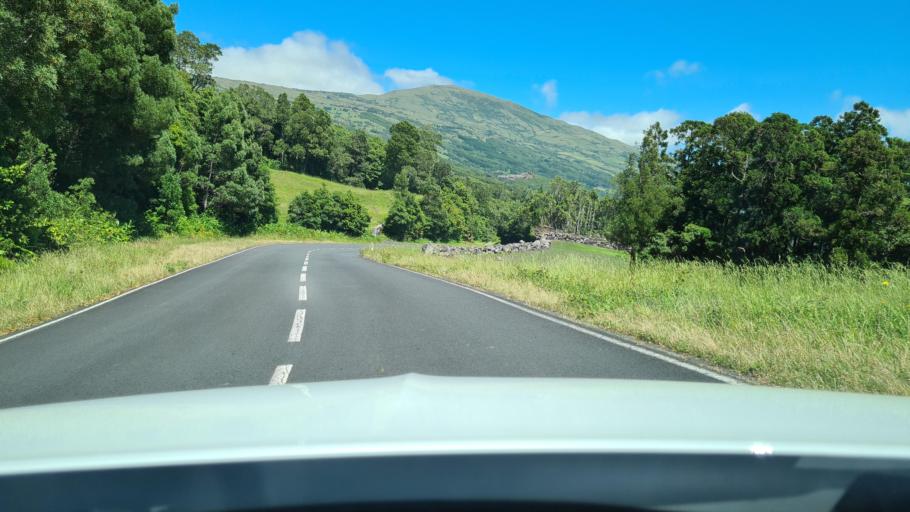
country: PT
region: Azores
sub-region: Sao Roque do Pico
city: Sao Roque do Pico
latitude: 38.4265
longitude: -28.2903
